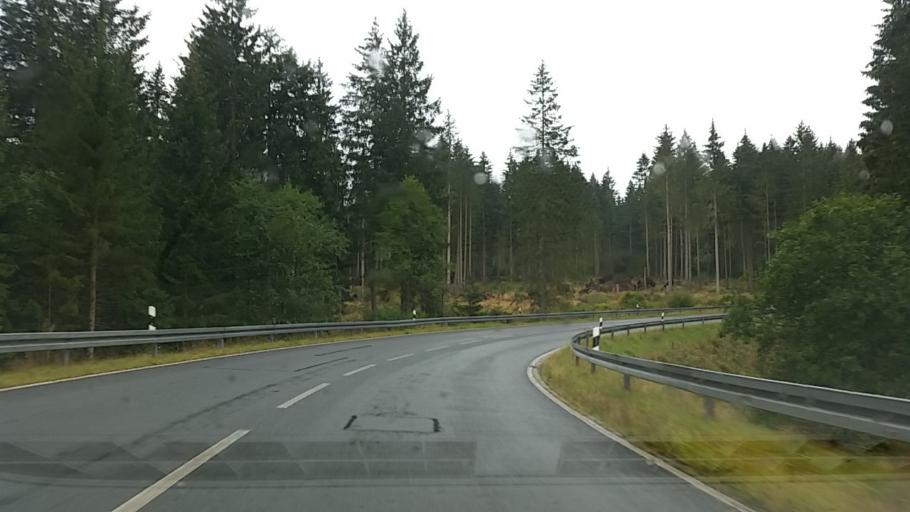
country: DE
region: Lower Saxony
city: Altenau
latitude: 51.7918
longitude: 10.4419
